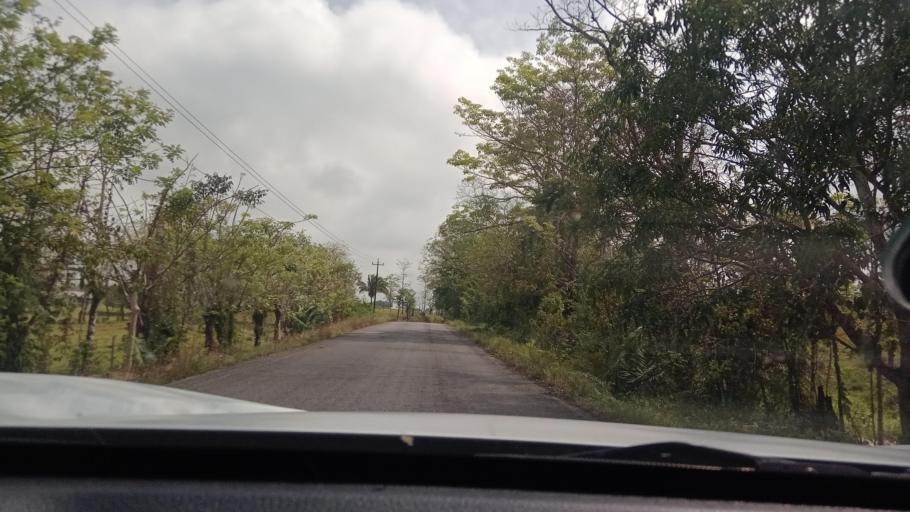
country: MX
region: Tabasco
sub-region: Huimanguillo
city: Francisco Rueda
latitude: 17.5722
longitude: -94.1085
